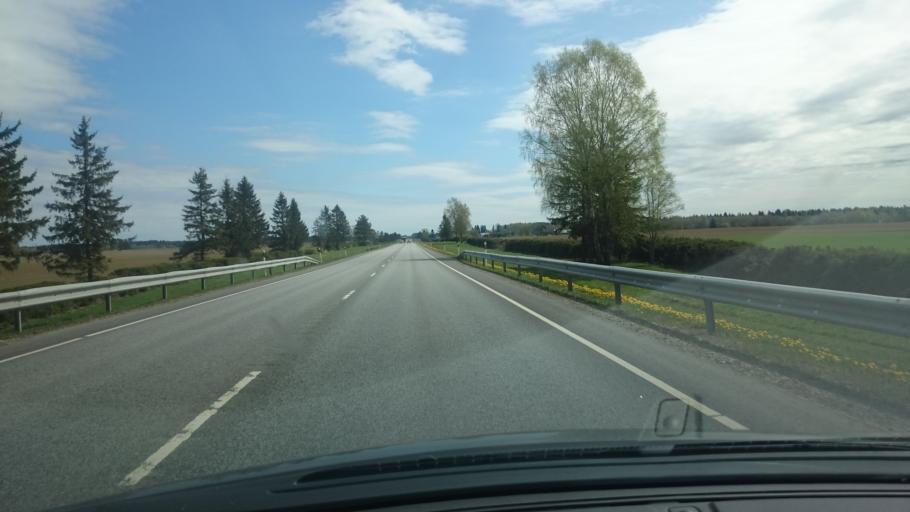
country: EE
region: Laeaene-Virumaa
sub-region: Someru vald
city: Someru
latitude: 59.3662
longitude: 26.4731
